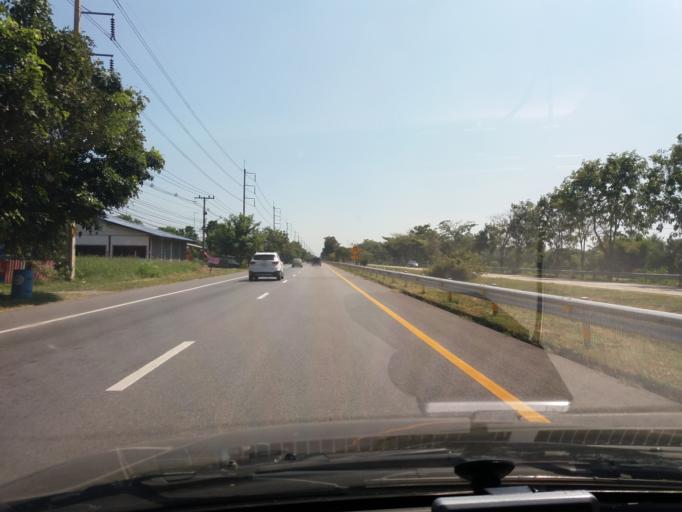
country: TH
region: Chai Nat
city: Chai Nat
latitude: 15.1351
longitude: 100.1446
